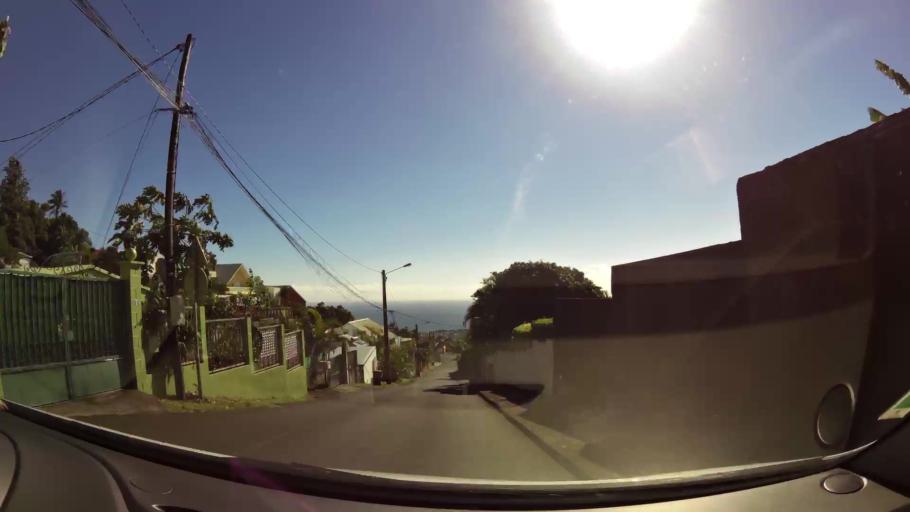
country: RE
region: Reunion
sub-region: Reunion
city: Saint-Denis
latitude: -20.9162
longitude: 55.4801
